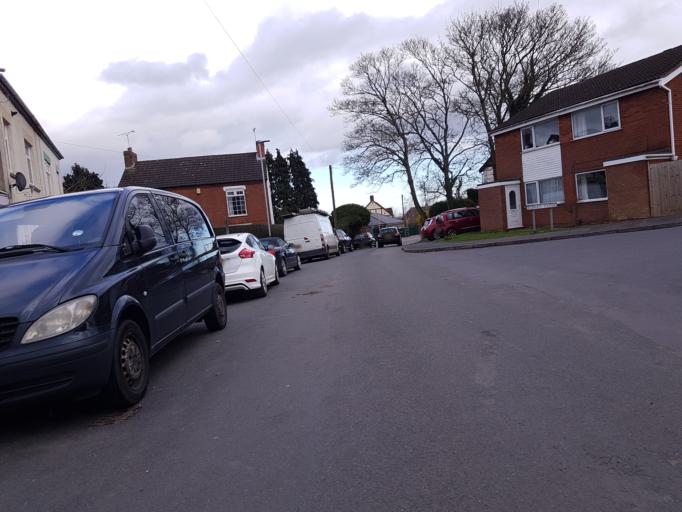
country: GB
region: England
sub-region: Leicestershire
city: Earl Shilton
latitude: 52.5793
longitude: -1.3043
